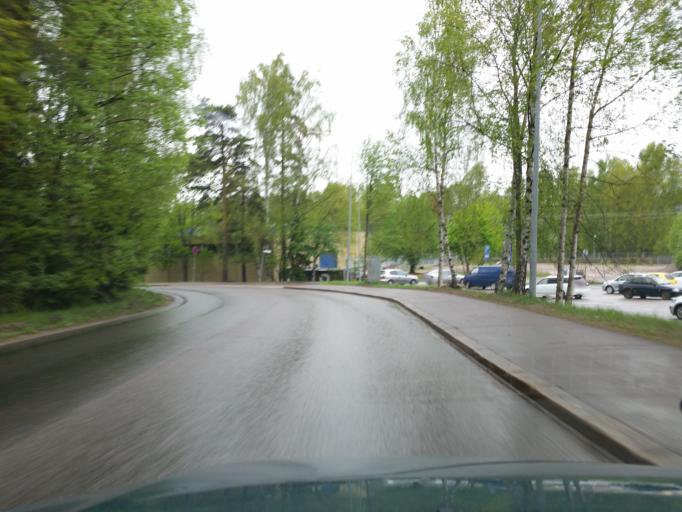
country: FI
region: Uusimaa
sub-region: Helsinki
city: Teekkarikylae
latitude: 60.2225
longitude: 24.8569
